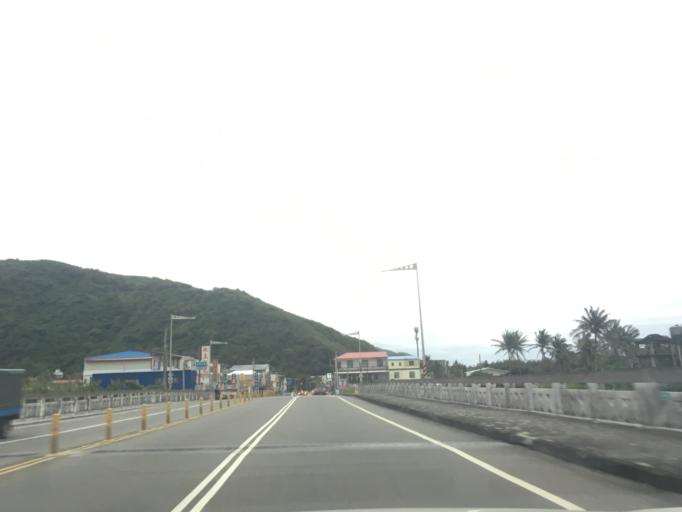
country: TW
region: Taiwan
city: Hengchun
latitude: 22.3606
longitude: 120.9070
